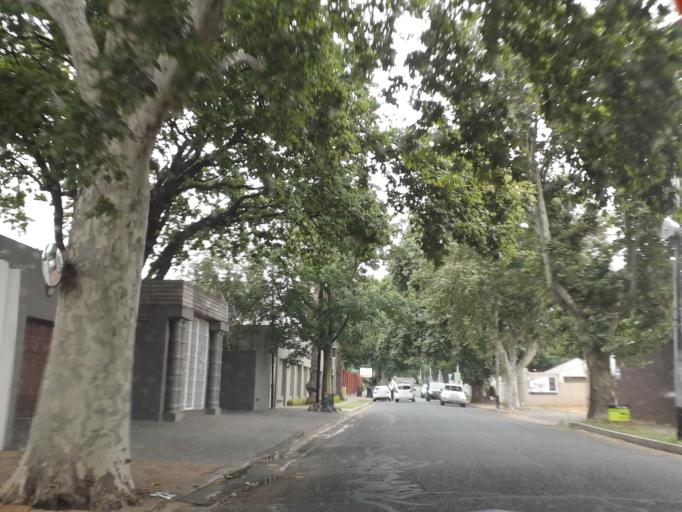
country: ZA
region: Gauteng
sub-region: City of Johannesburg Metropolitan Municipality
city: Johannesburg
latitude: -26.1620
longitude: 28.0750
